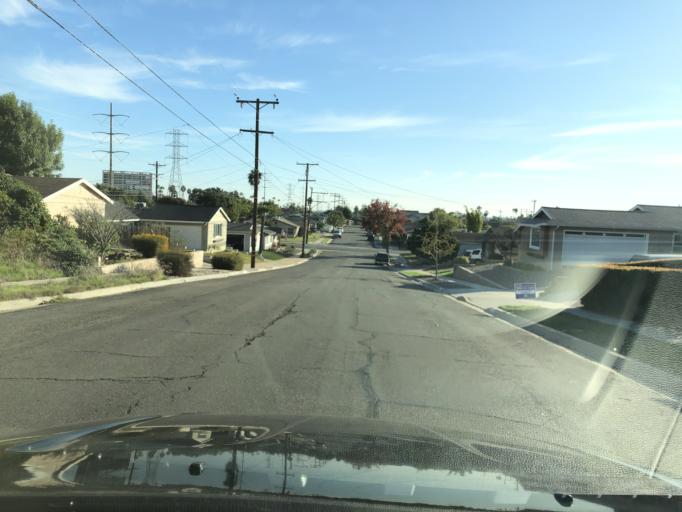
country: US
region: California
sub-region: San Diego County
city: La Jolla
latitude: 32.8219
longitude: -117.1854
